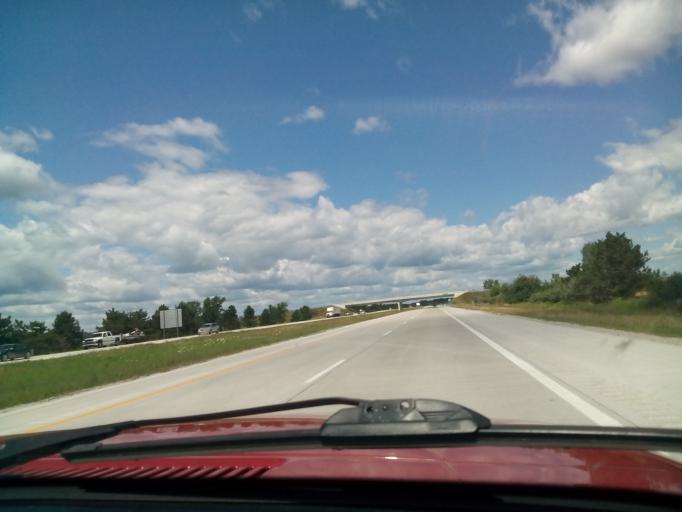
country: US
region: Michigan
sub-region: Bay County
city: Pinconning
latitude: 43.8651
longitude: -84.0211
